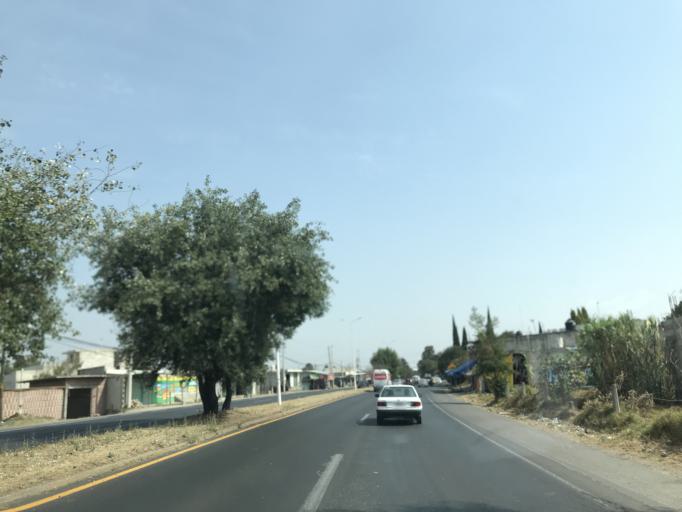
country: MX
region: Tlaxcala
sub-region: Teolocholco
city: Teolocholco
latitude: 19.2575
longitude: -98.2003
